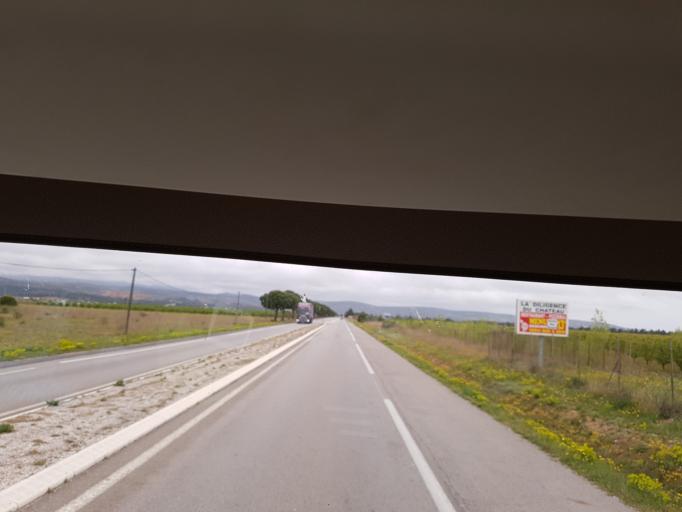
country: FR
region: Languedoc-Roussillon
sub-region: Departement des Pyrenees-Orientales
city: Salses-le-Chateau
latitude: 42.8095
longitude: 2.9129
